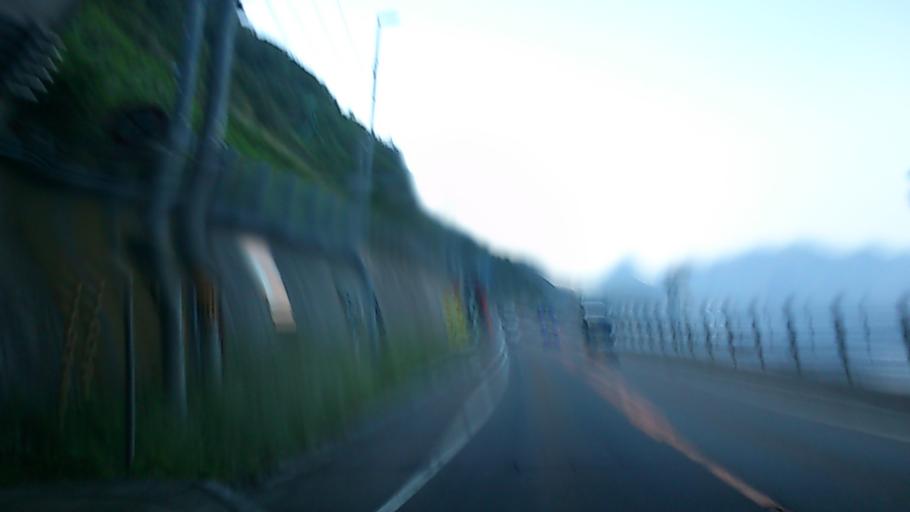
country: JP
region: Hokkaido
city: Kamiiso
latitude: 41.4096
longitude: 140.2149
